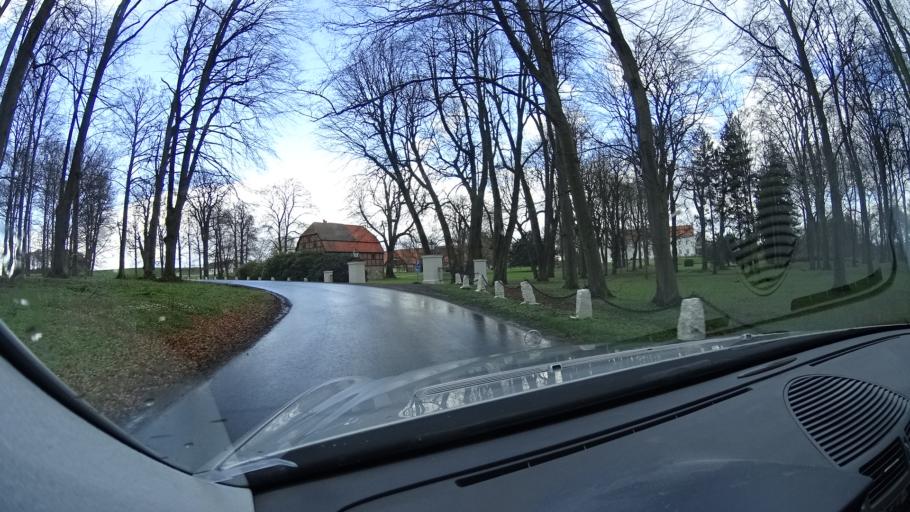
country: SE
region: Skane
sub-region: Eslovs Kommun
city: Eslov
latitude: 55.8106
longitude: 13.2847
